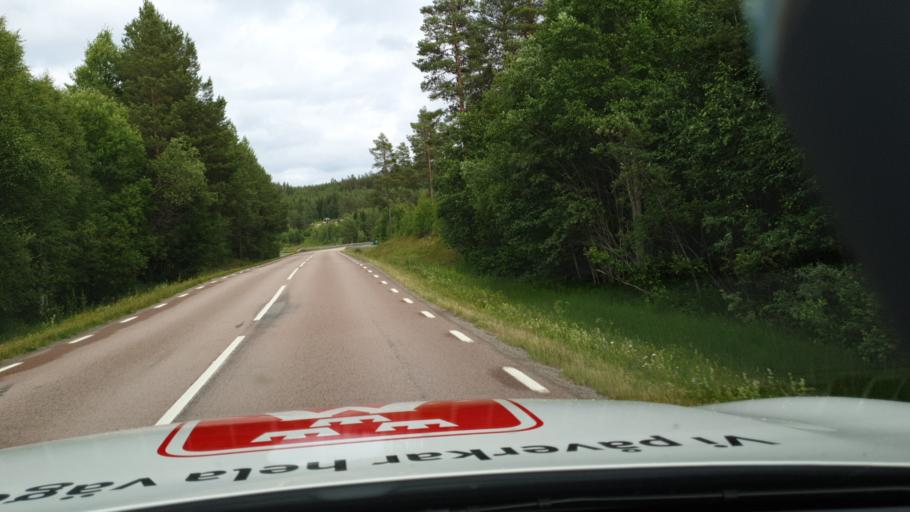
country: SE
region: Vaesternorrland
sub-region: Solleftea Kommun
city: As
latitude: 63.6004
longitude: 16.2167
